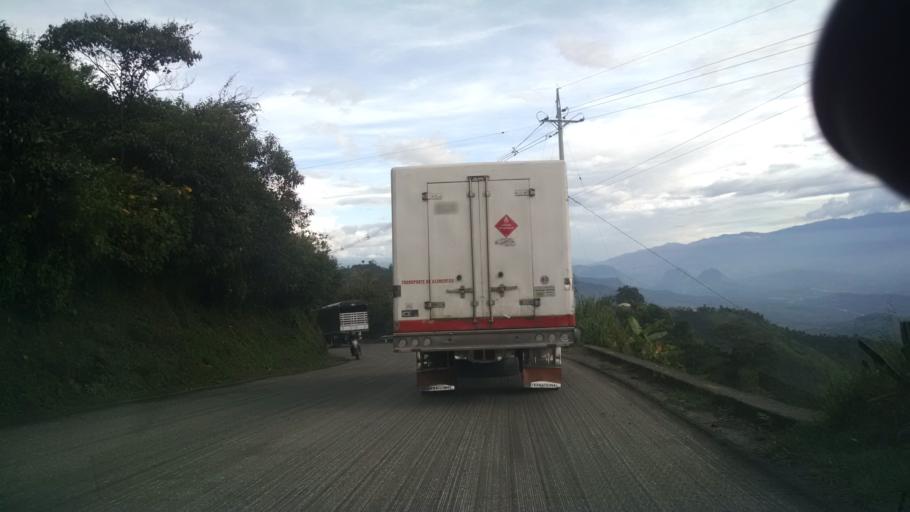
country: CO
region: Antioquia
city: Santa Barbara
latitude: 5.9133
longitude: -75.5766
